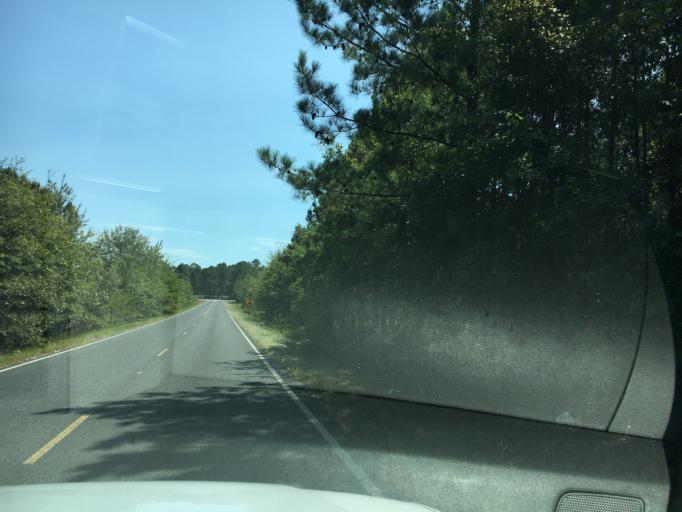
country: US
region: South Carolina
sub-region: Lexington County
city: Batesburg
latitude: 33.8007
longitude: -81.6430
